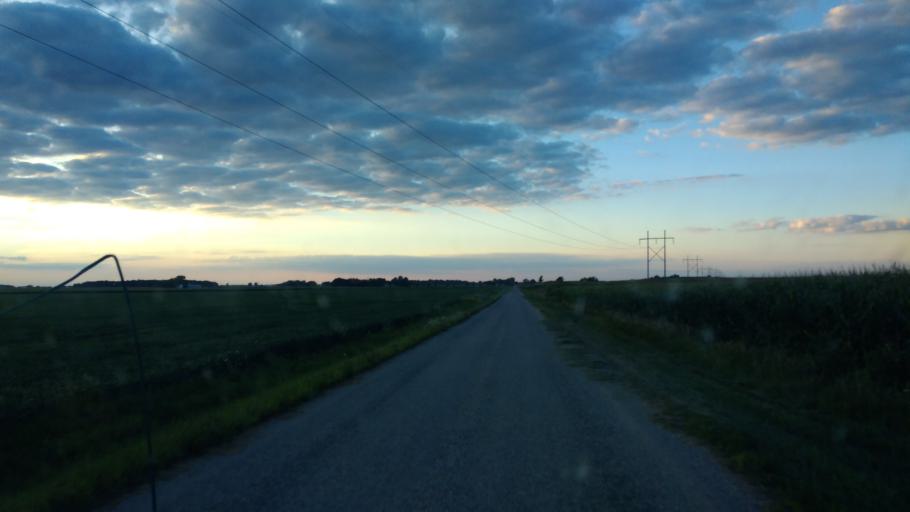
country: US
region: Indiana
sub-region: Adams County
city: Geneva
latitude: 40.6144
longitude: -85.0600
